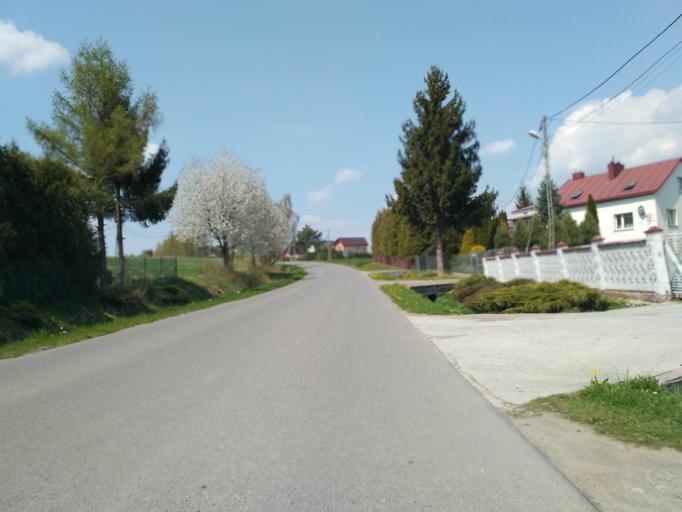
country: PL
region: Subcarpathian Voivodeship
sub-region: Powiat jasielski
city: Tarnowiec
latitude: 49.6700
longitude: 21.5573
